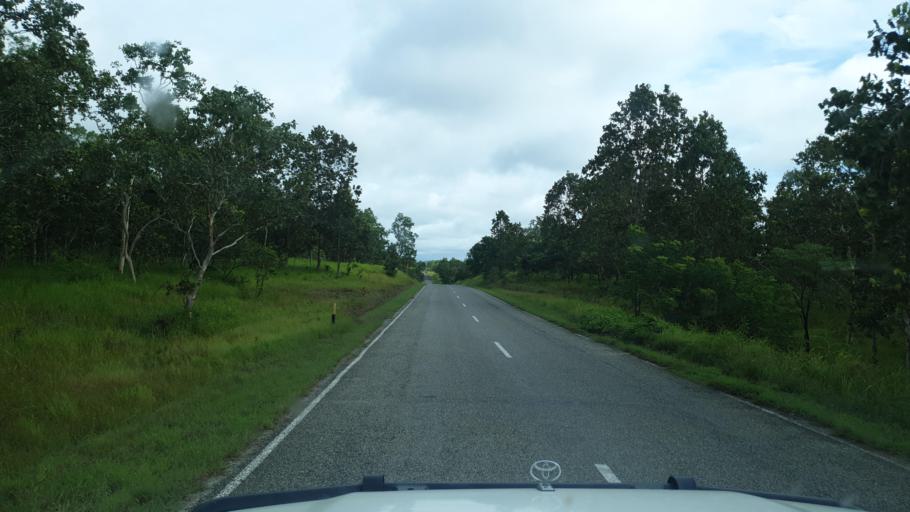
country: PG
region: National Capital
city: Port Moresby
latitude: -8.8461
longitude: 146.6832
